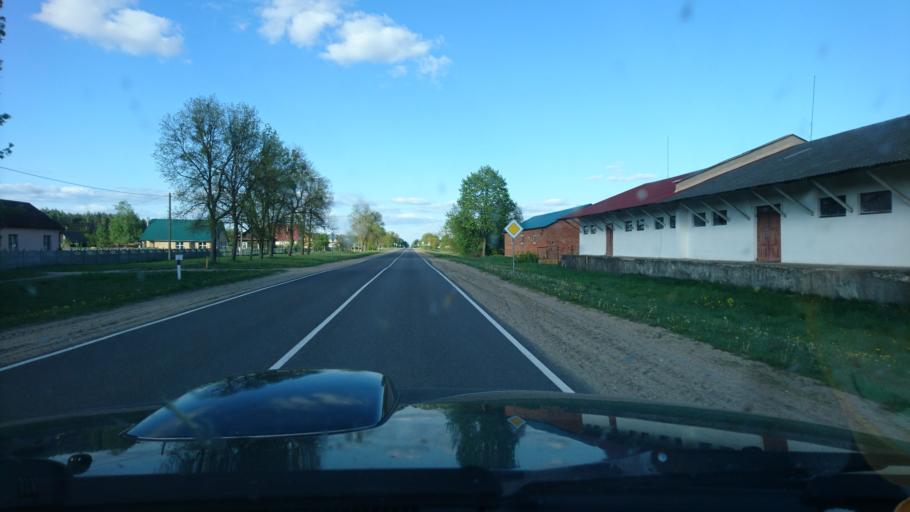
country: BY
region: Brest
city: Nyakhachava
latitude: 52.6471
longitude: 25.2119
